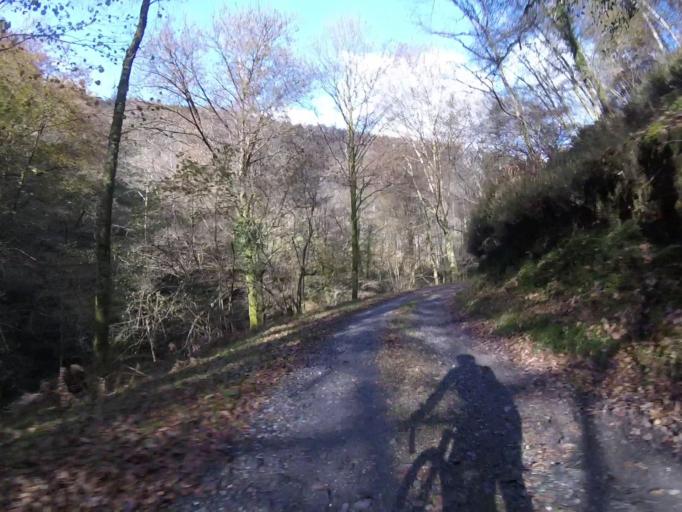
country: ES
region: Navarre
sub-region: Provincia de Navarra
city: Goizueta
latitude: 43.2100
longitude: -1.8123
